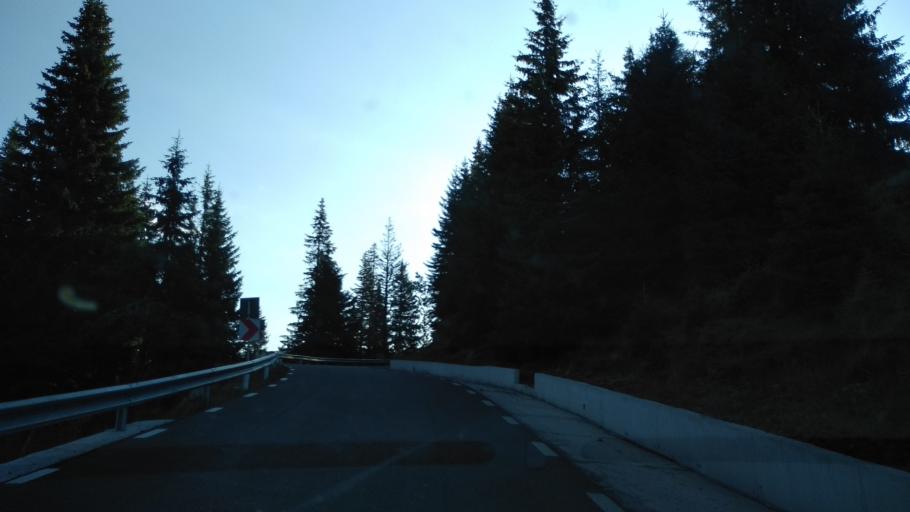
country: RO
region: Prahova
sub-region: Oras Sinaia
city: Sinaia
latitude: 45.3391
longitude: 25.4611
